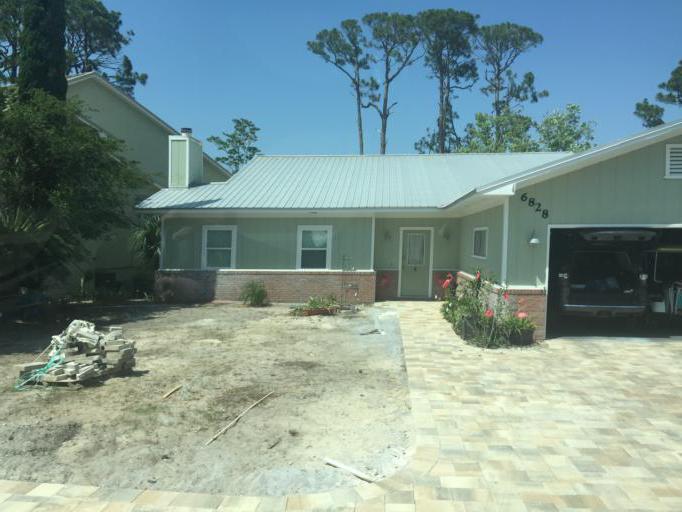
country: US
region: Florida
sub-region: Bay County
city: Lower Grand Lagoon
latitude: 30.1580
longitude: -85.7696
